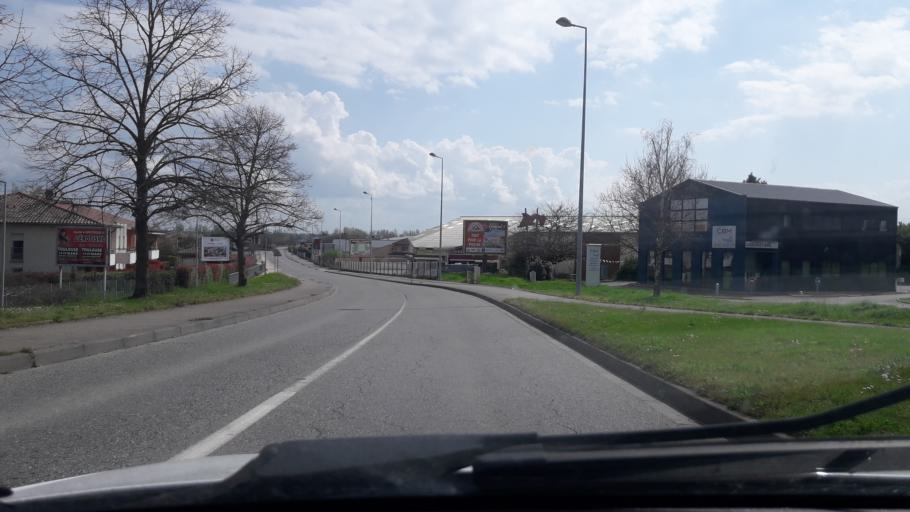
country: FR
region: Midi-Pyrenees
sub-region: Departement de la Haute-Garonne
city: Seysses
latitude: 43.4932
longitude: 1.3133
